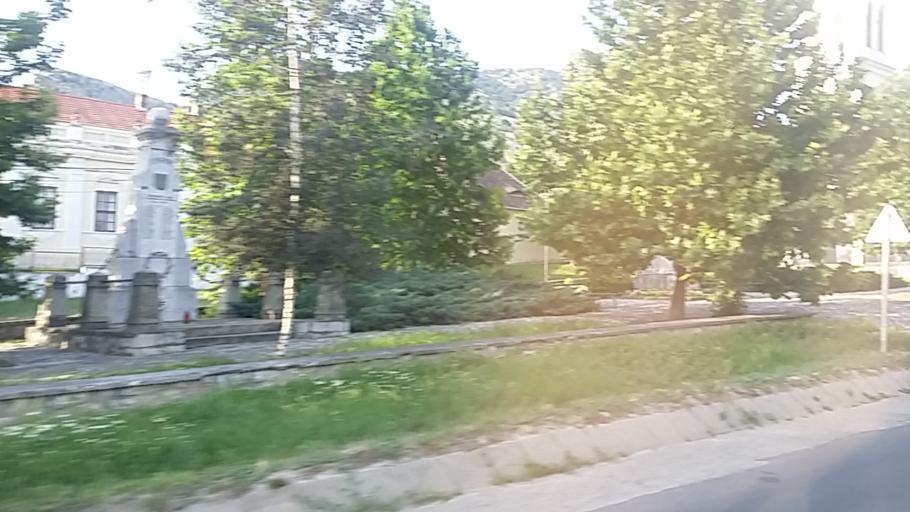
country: HU
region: Baranya
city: Villany
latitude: 45.8474
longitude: 18.3990
